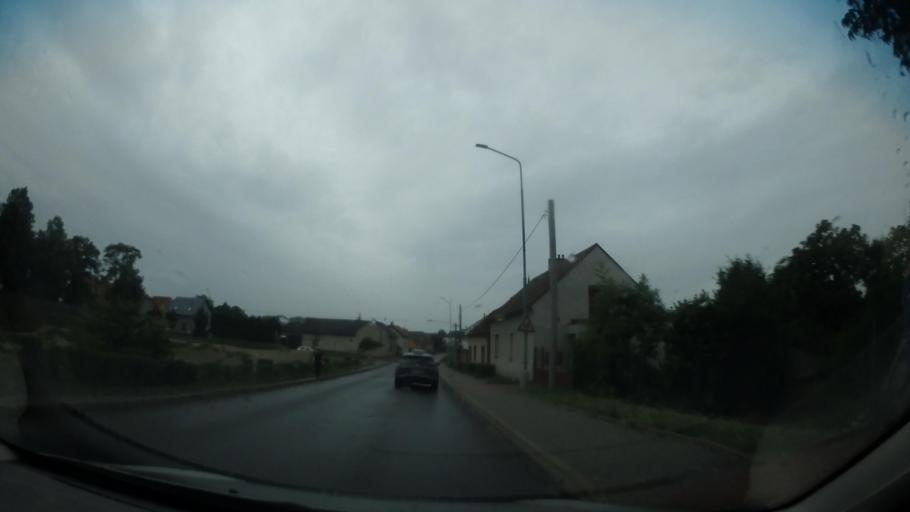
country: CZ
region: Central Bohemia
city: Milovice
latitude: 50.2298
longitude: 14.8854
